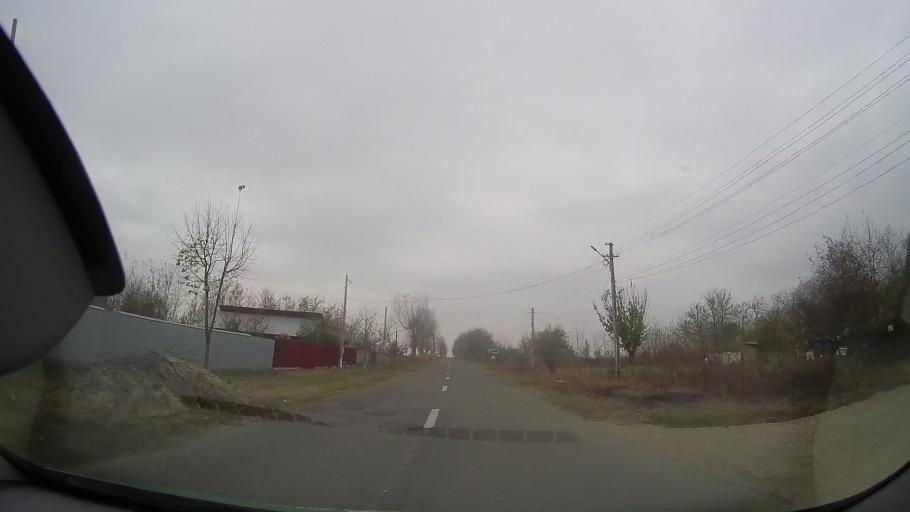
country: RO
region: Ialomita
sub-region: Comuna Grindu
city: Grindu
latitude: 44.7705
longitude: 26.8955
